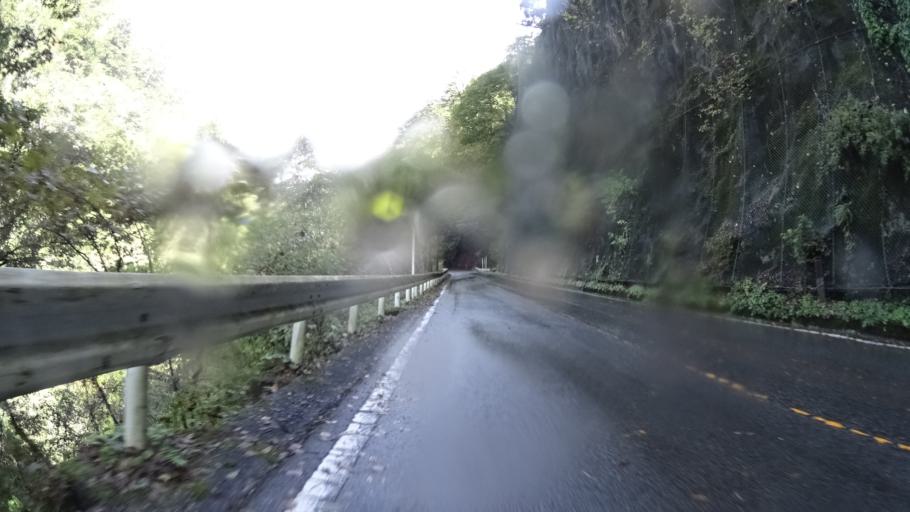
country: JP
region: Yamanashi
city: Enzan
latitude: 35.7958
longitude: 138.8658
